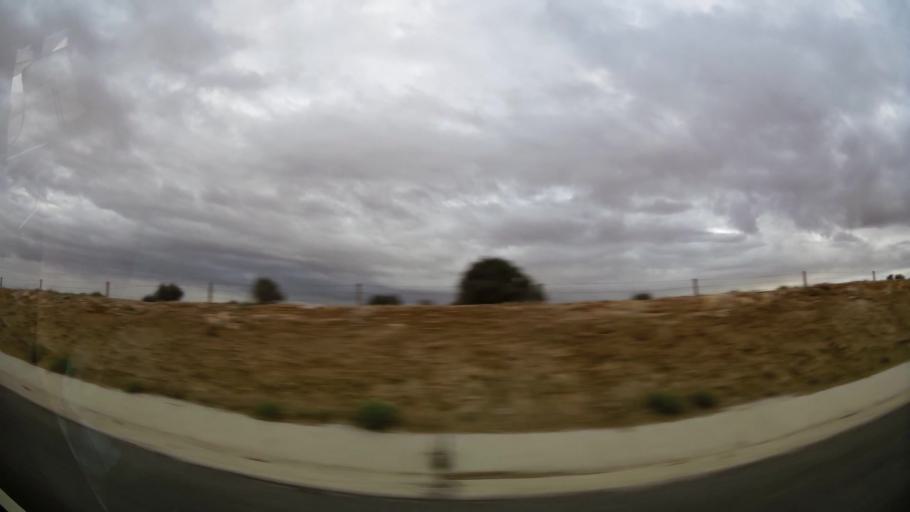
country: MA
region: Taza-Al Hoceima-Taounate
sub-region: Taza
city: Guercif
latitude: 34.3052
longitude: -3.6381
